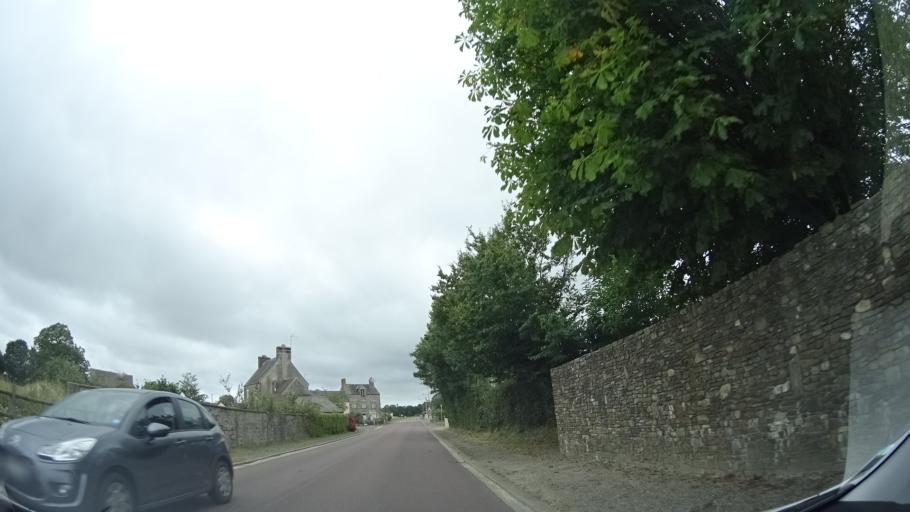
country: FR
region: Lower Normandy
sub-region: Departement de la Manche
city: La Haye-du-Puits
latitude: 49.3007
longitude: -1.5748
